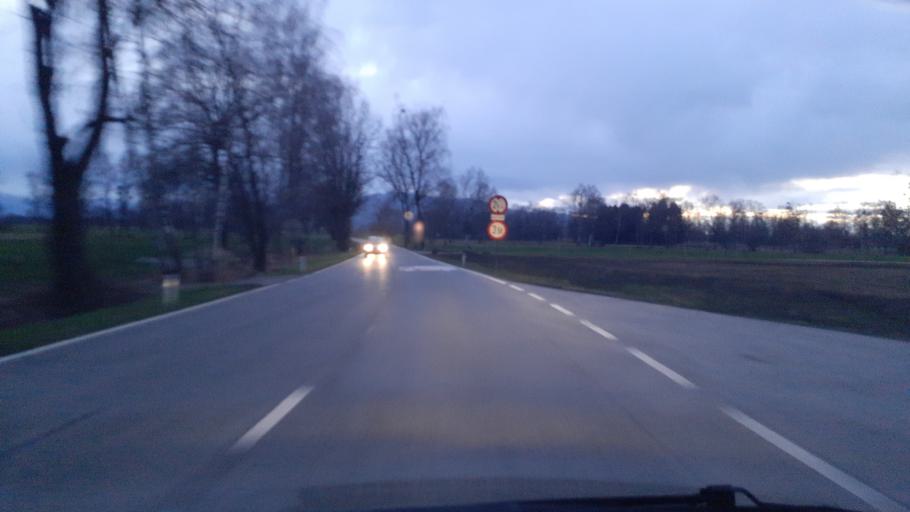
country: AT
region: Vorarlberg
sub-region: Politischer Bezirk Bregenz
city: Lauterach
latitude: 47.4572
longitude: 9.7136
